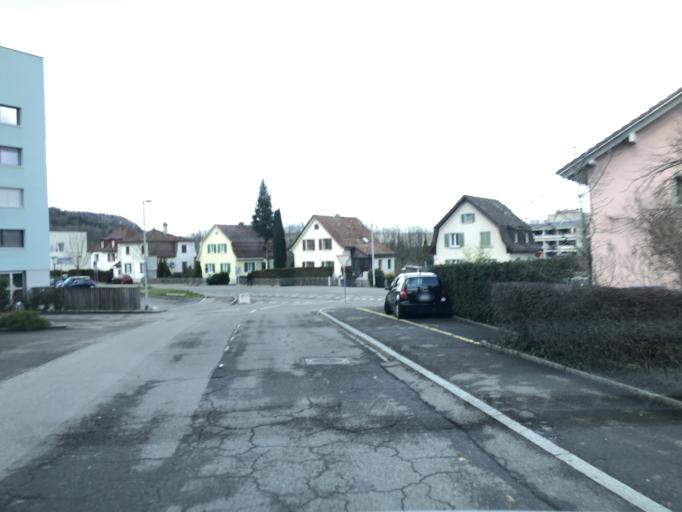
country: CH
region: Aargau
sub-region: Bezirk Baden
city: Obersiggenthal
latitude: 47.4826
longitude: 8.2813
